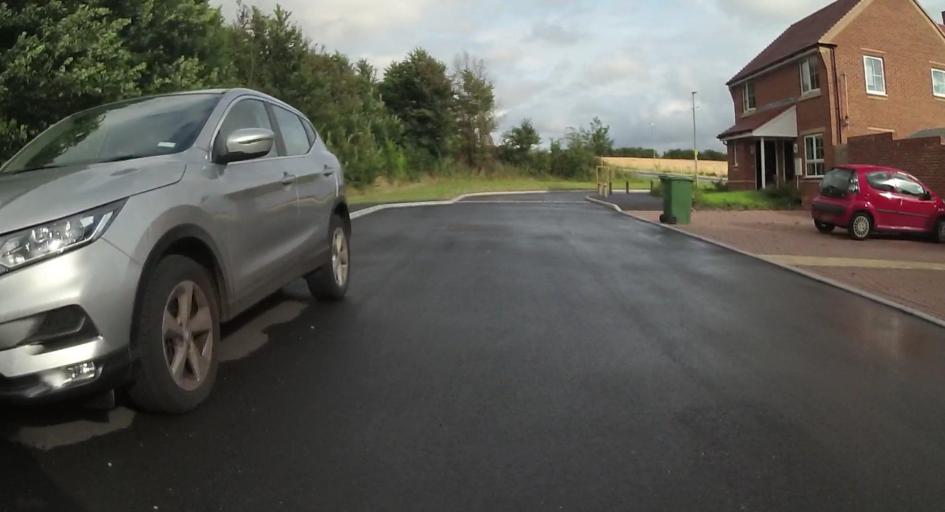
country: GB
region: England
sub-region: Hampshire
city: Overton
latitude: 51.2220
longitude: -1.3343
